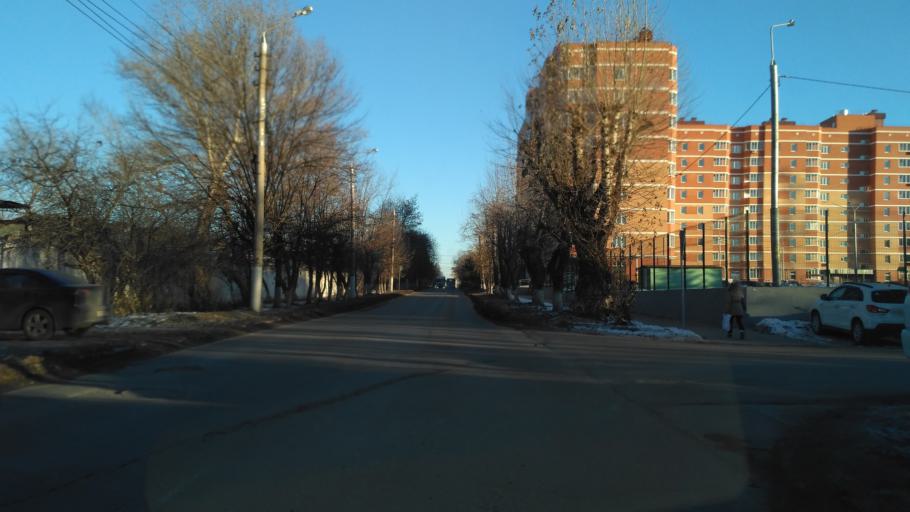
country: RU
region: Tula
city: Tula
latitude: 54.2098
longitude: 37.6119
